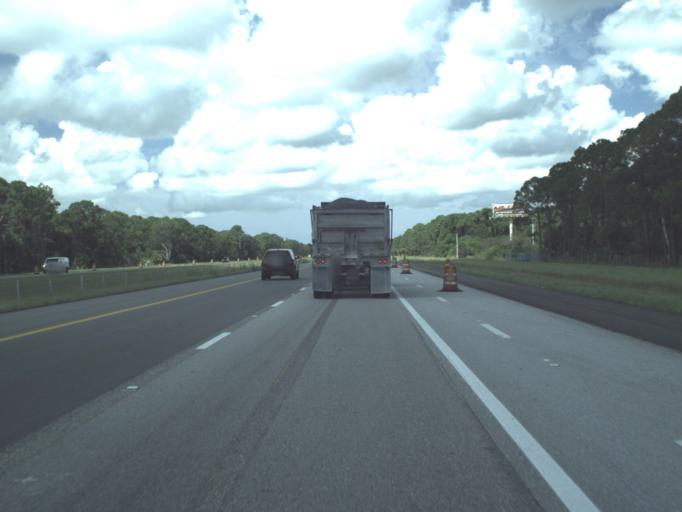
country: US
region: Florida
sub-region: Sarasota County
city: Warm Mineral Springs
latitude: 27.1000
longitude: -82.2462
